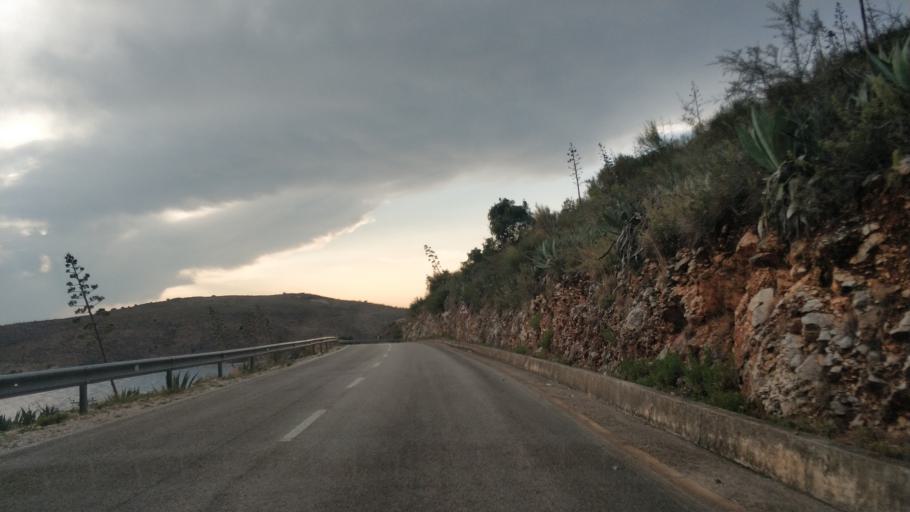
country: AL
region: Vlore
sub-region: Rrethi i Vlores
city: Himare
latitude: 40.0690
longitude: 19.7908
